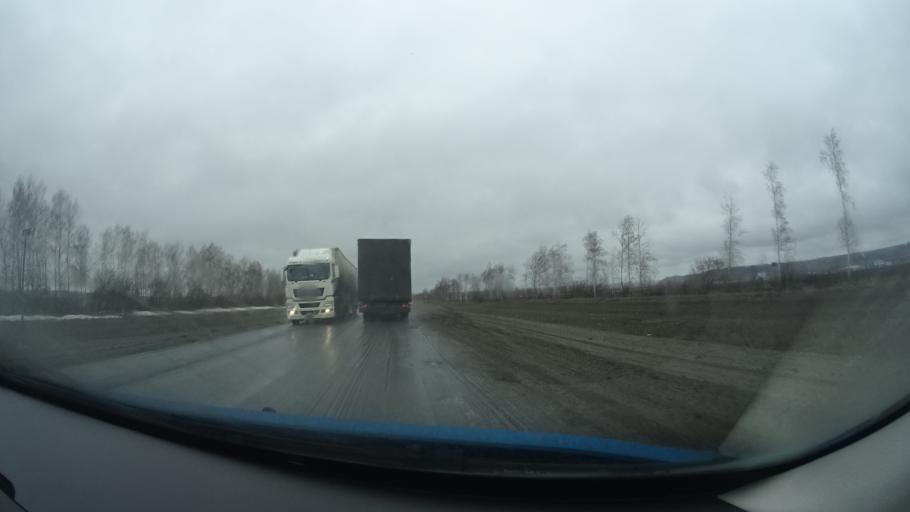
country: RU
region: Bashkortostan
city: Kandry
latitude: 54.5373
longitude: 54.1248
